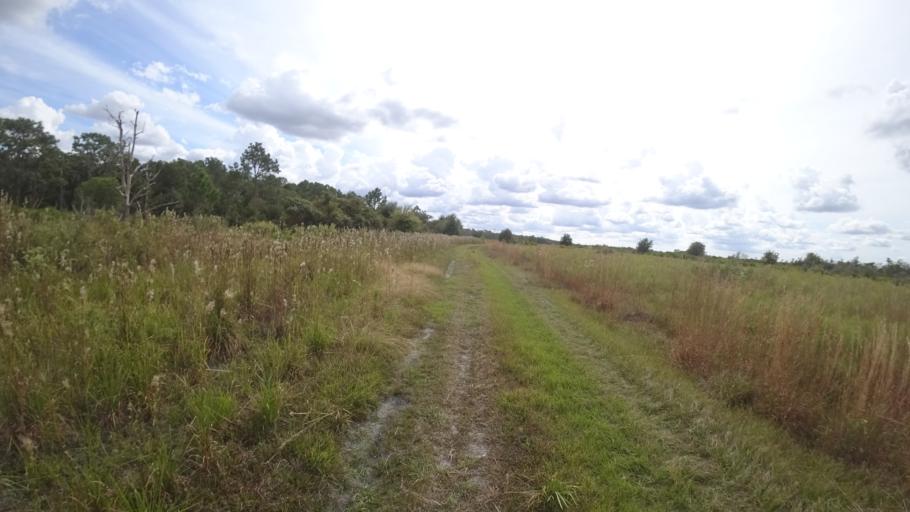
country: US
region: Florida
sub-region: Hillsborough County
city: Wimauma
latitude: 27.5481
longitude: -82.1354
